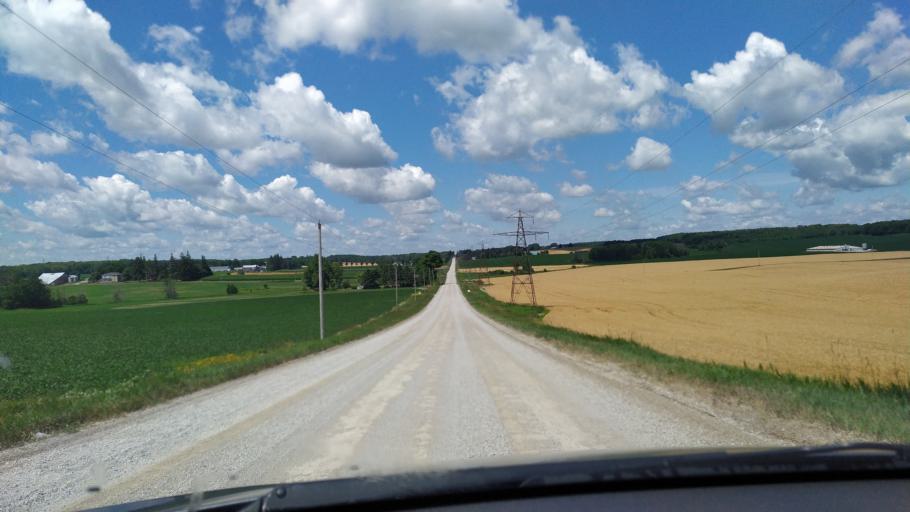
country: CA
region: Ontario
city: Stratford
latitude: 43.3874
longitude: -80.7622
